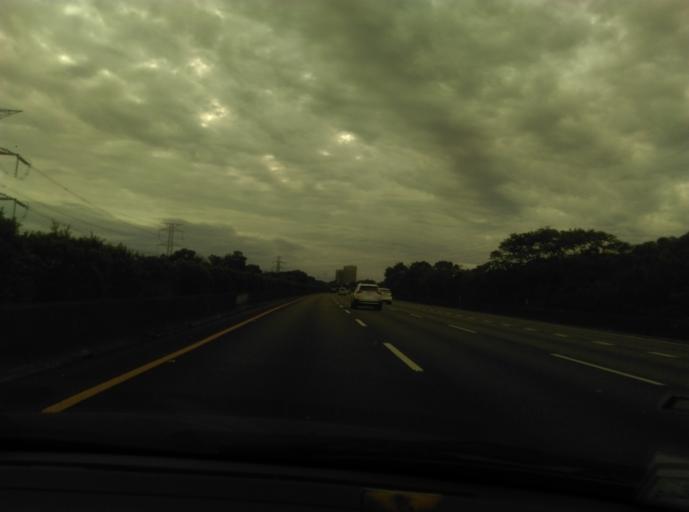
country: TW
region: Taiwan
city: Daxi
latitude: 24.9152
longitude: 121.2944
